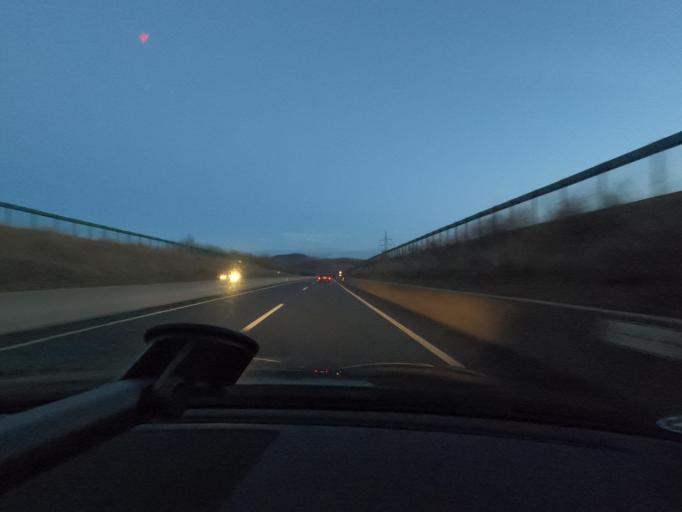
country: DE
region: Lower Saxony
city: Bad Lauterberg im Harz
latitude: 51.6116
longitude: 10.4589
